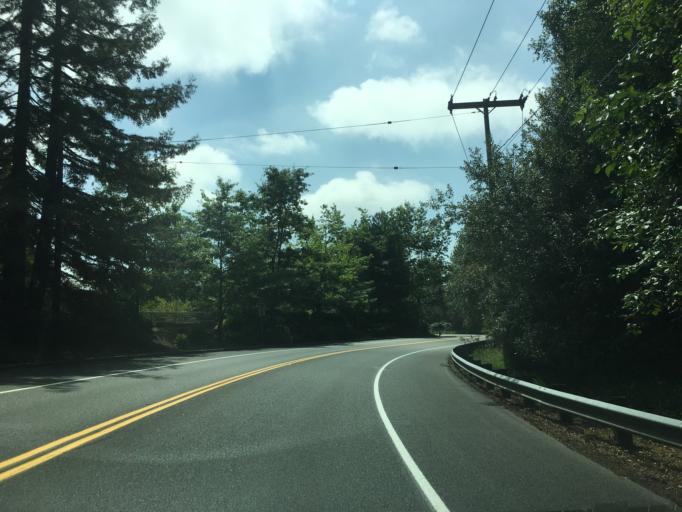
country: US
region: Washington
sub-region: King County
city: Inglewood-Finn Hill
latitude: 47.7198
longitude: -122.2373
